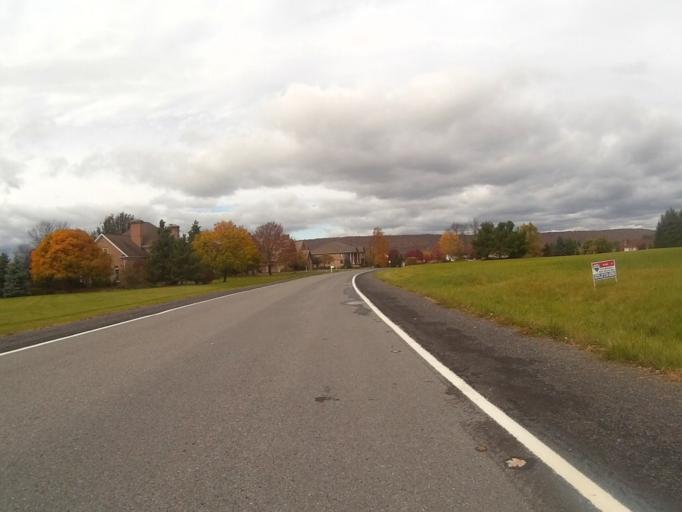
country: US
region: Pennsylvania
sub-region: Centre County
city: Boalsburg
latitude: 40.7756
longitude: -77.7620
